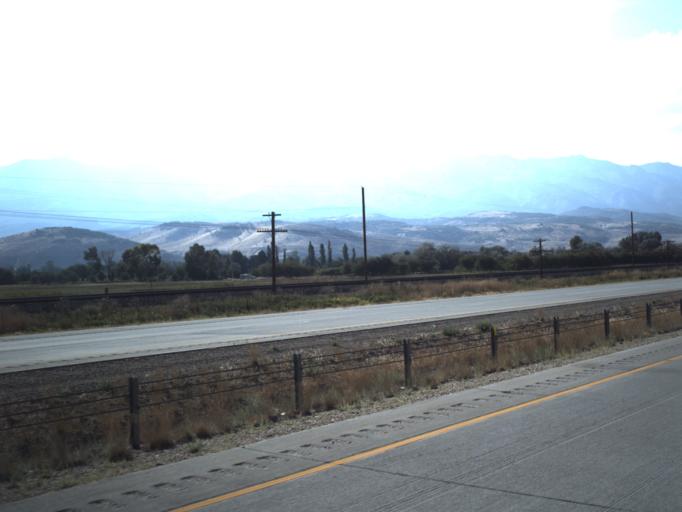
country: US
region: Utah
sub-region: Morgan County
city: Morgan
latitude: 41.0611
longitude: -111.7034
